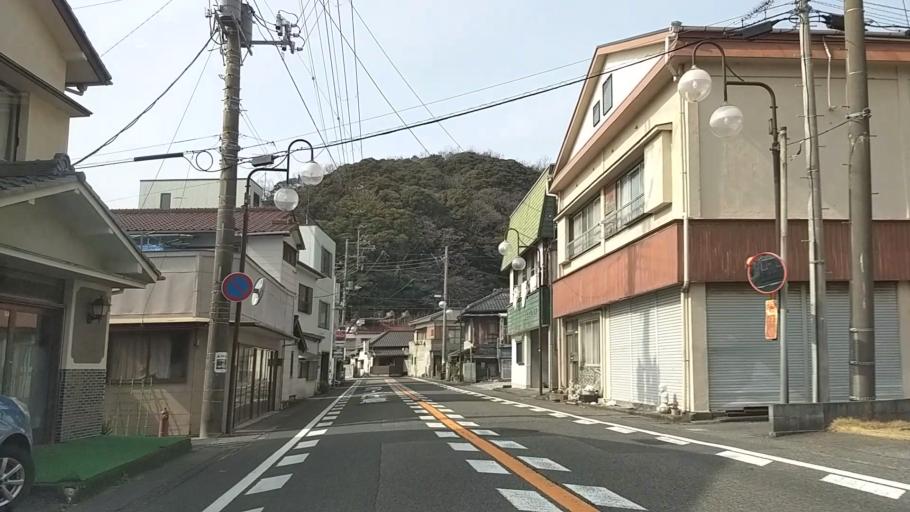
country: JP
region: Shizuoka
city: Heda
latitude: 34.9149
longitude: 138.7900
